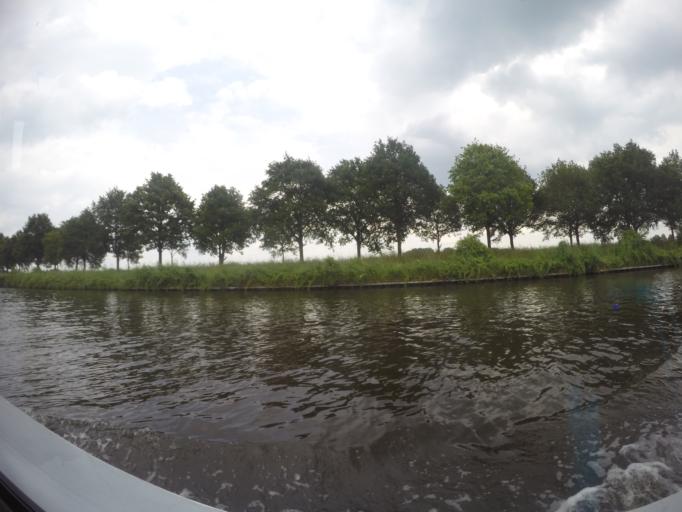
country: NL
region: Overijssel
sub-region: Gemeente Hof van Twente
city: Delden
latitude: 52.2667
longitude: 6.6447
